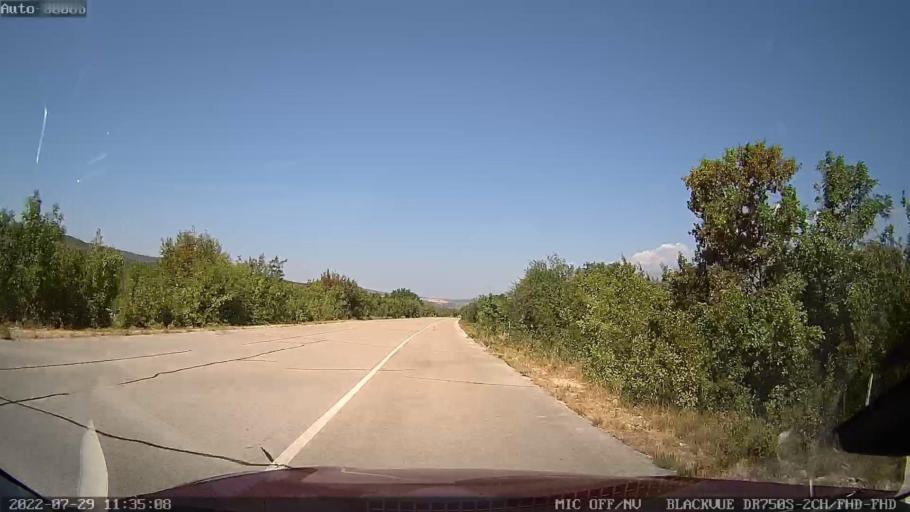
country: HR
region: Zadarska
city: Obrovac
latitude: 44.1808
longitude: 15.7173
